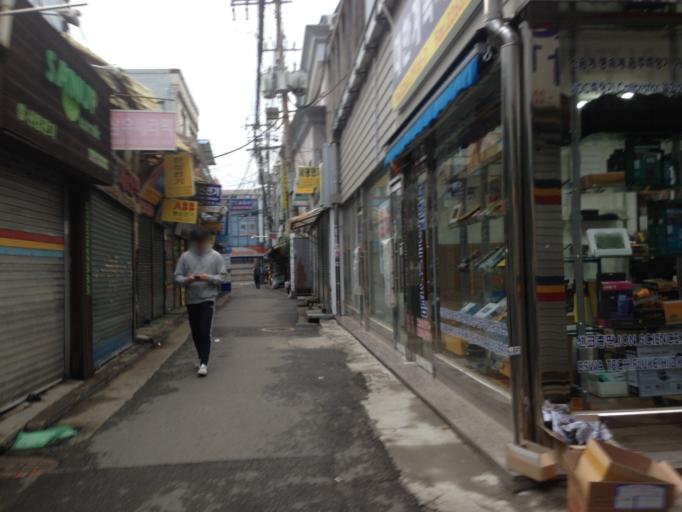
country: KR
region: Seoul
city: Seoul
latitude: 37.5693
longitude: 126.9926
